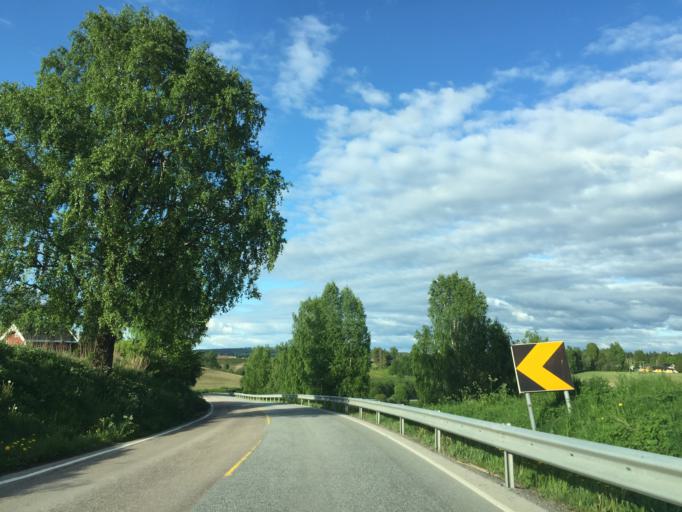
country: NO
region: Akershus
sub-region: Sorum
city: Sorumsand
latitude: 59.9844
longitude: 11.2738
